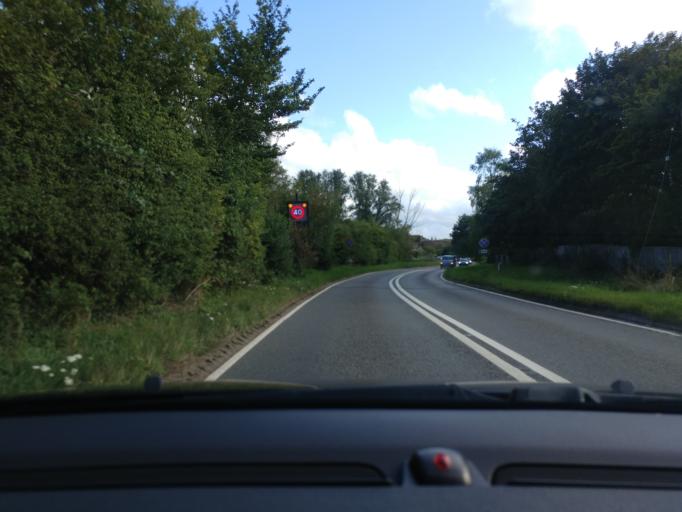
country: GB
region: England
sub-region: Oxfordshire
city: Kidlington
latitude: 51.8680
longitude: -1.2270
